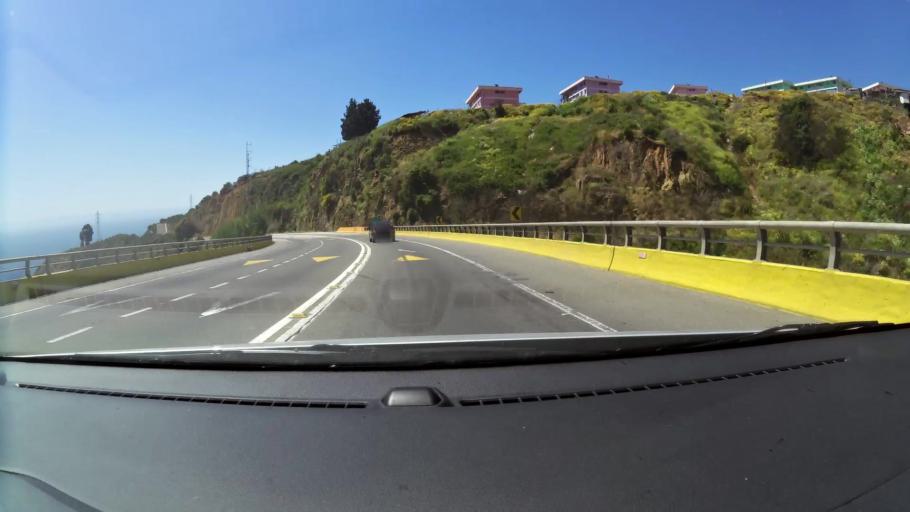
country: CL
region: Valparaiso
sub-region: Provincia de Valparaiso
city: Valparaiso
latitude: -33.0556
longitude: -71.6532
